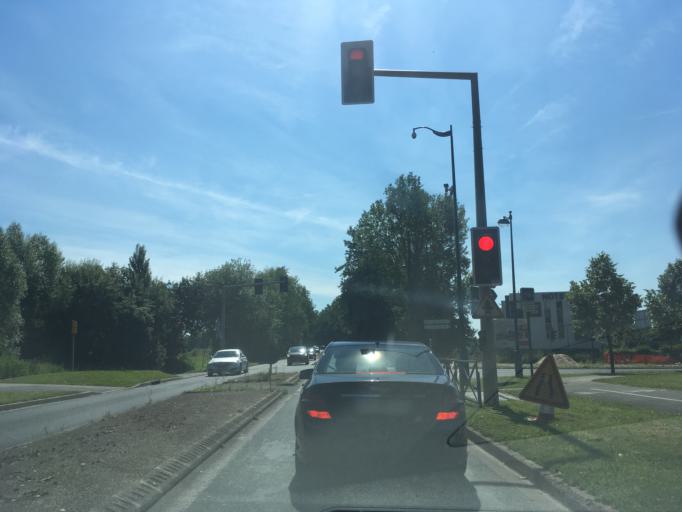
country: FR
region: Ile-de-France
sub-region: Departement de Seine-et-Marne
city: Bailly-Romainvilliers
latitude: 48.8500
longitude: 2.8290
